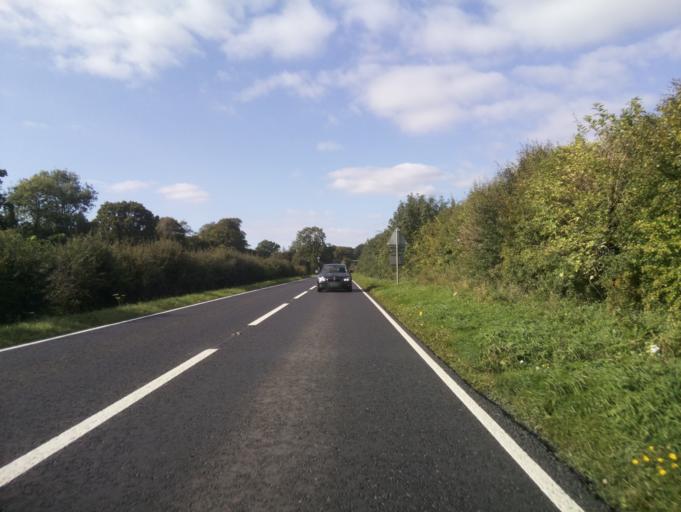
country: GB
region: England
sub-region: Hampshire
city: Four Marks
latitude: 51.1785
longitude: -1.0577
